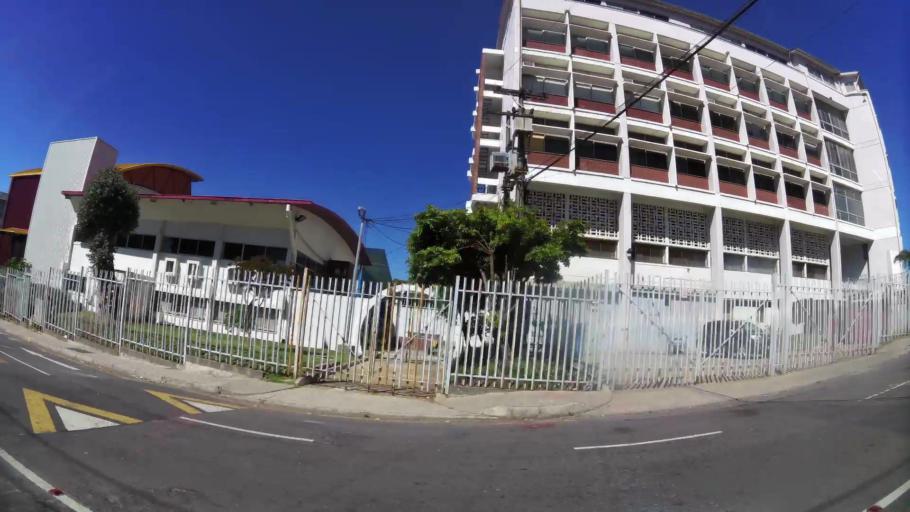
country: CL
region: Valparaiso
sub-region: Provincia de Valparaiso
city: Valparaiso
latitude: -33.0242
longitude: -71.6413
